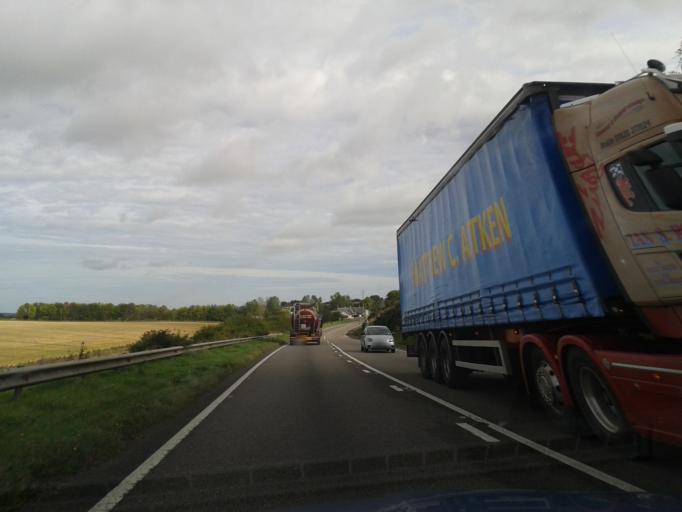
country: GB
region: Scotland
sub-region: Moray
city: Burghead
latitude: 57.6380
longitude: -3.4616
